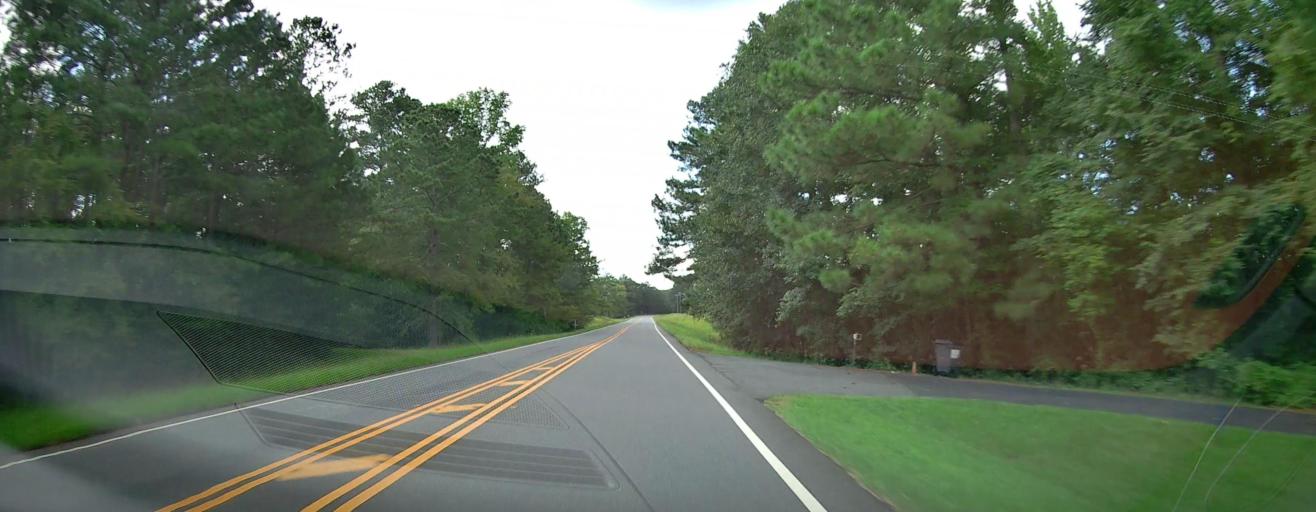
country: US
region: Georgia
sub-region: Bibb County
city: West Point
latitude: 32.8750
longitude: -83.9228
